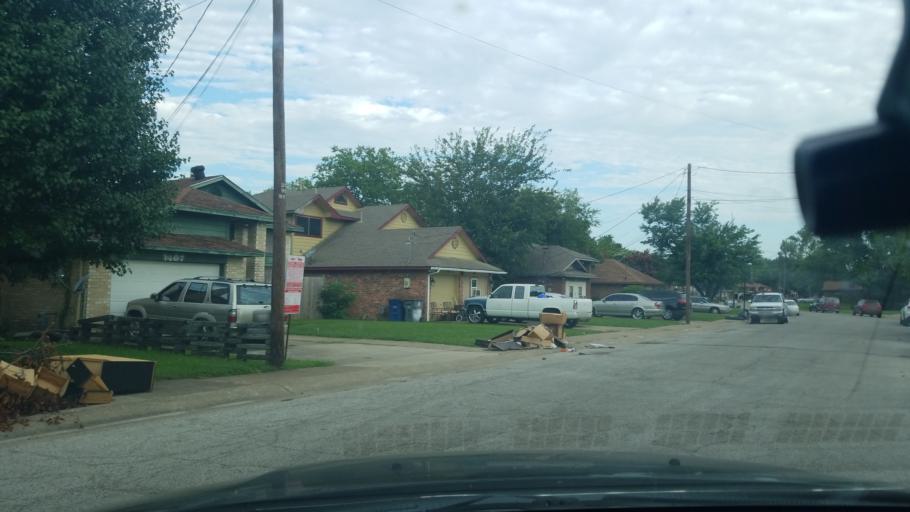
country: US
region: Texas
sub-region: Dallas County
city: Balch Springs
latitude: 32.7370
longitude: -96.6615
